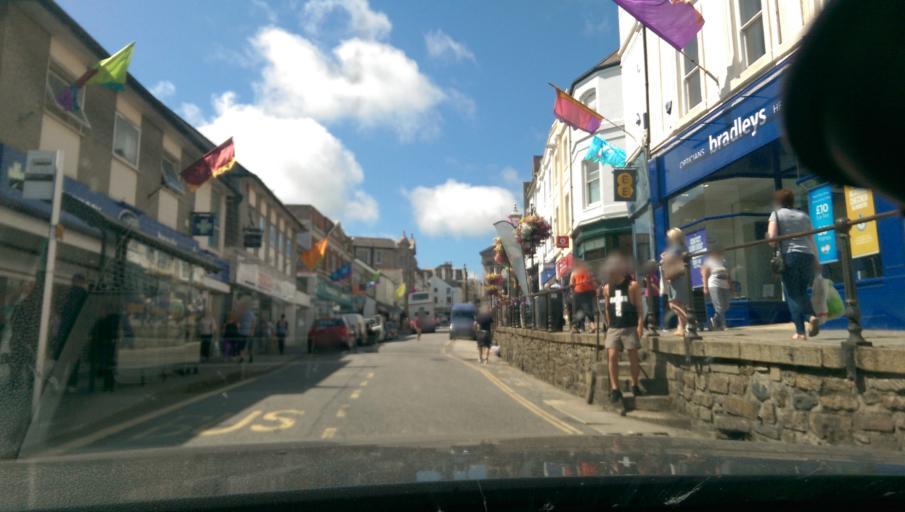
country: GB
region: England
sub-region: Cornwall
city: Penzance
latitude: 50.1198
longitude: -5.5351
